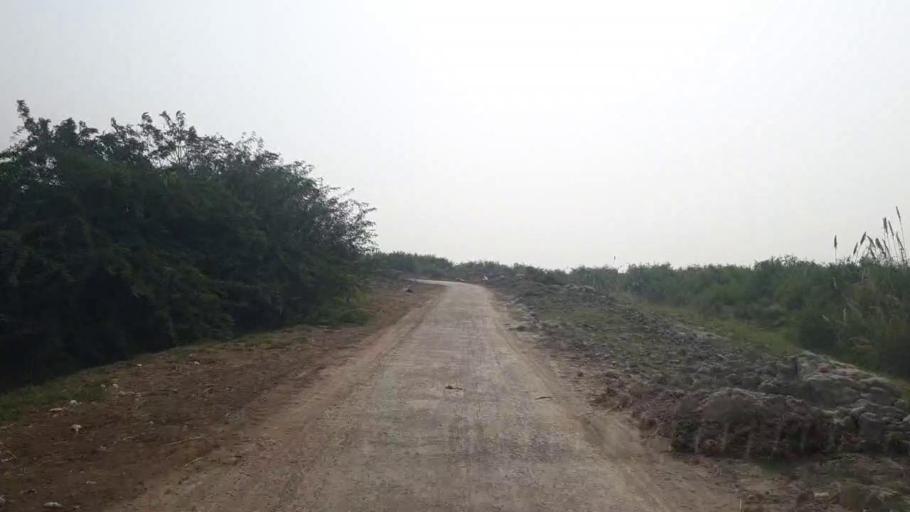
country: PK
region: Sindh
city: Tando Muhammad Khan
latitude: 25.2685
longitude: 68.5001
